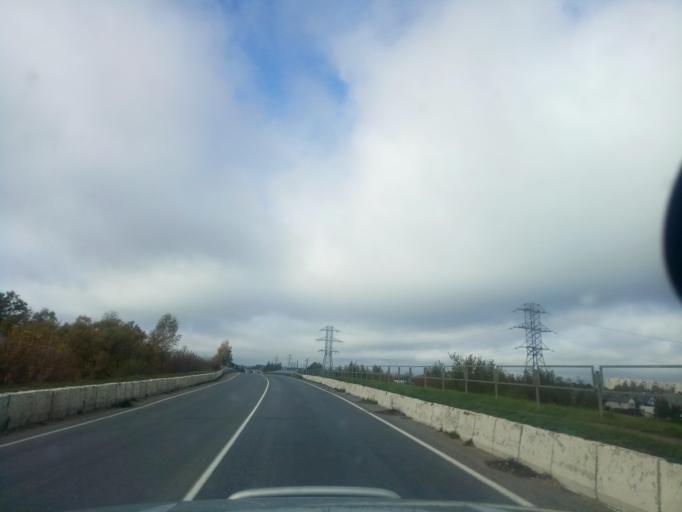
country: BY
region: Minsk
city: Zaslawye
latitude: 53.9990
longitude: 27.2848
